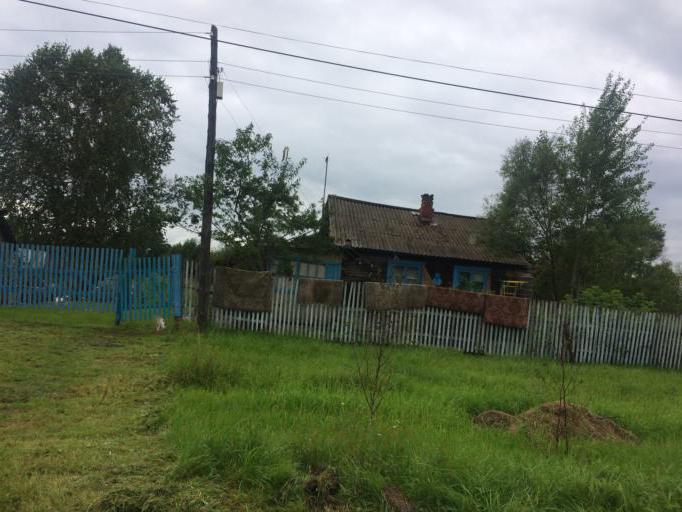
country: RU
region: Primorskiy
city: Lazo
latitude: 45.8814
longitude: 133.6541
